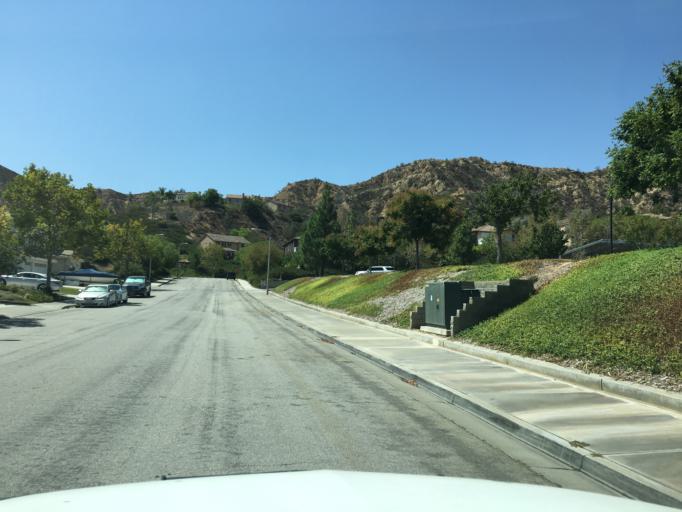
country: US
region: California
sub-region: Los Angeles County
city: Castaic
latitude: 34.4717
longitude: -118.6301
